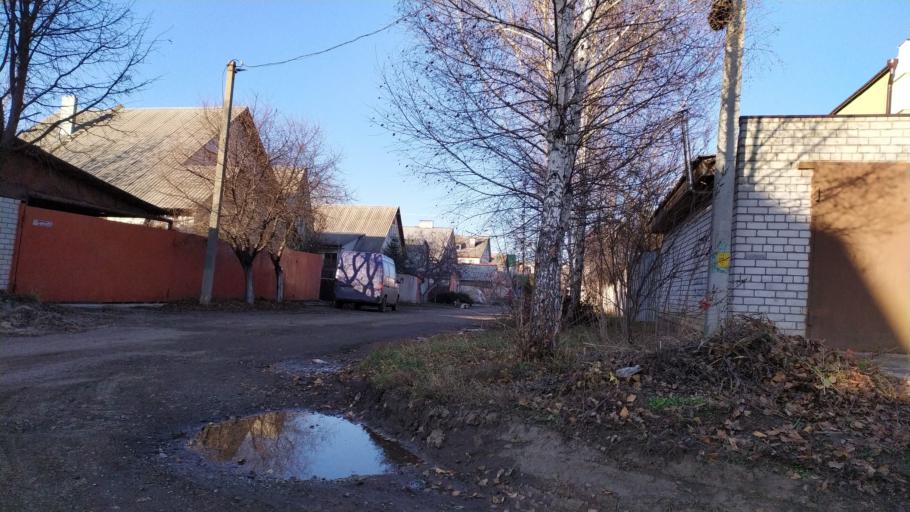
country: RU
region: Kursk
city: Kursk
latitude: 51.6444
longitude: 36.1380
